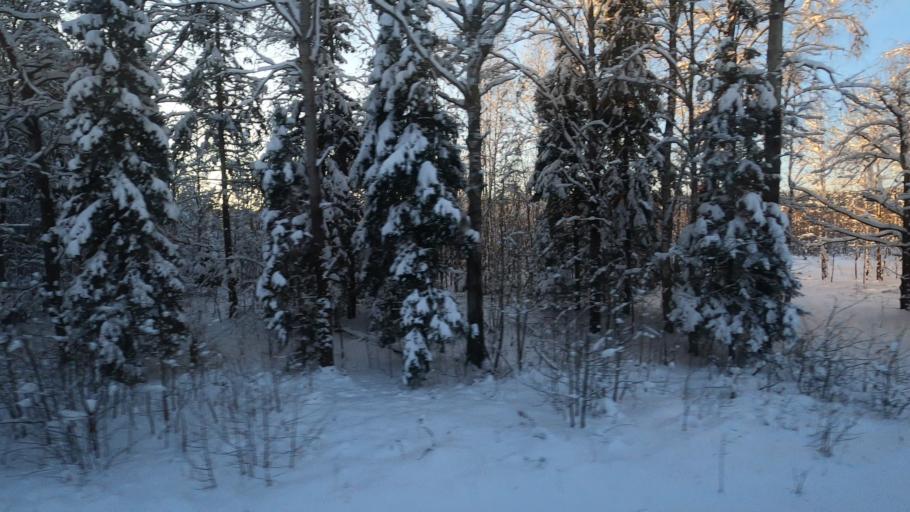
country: RU
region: Moskovskaya
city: Novo-Nikol'skoye
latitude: 56.6341
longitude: 37.5626
